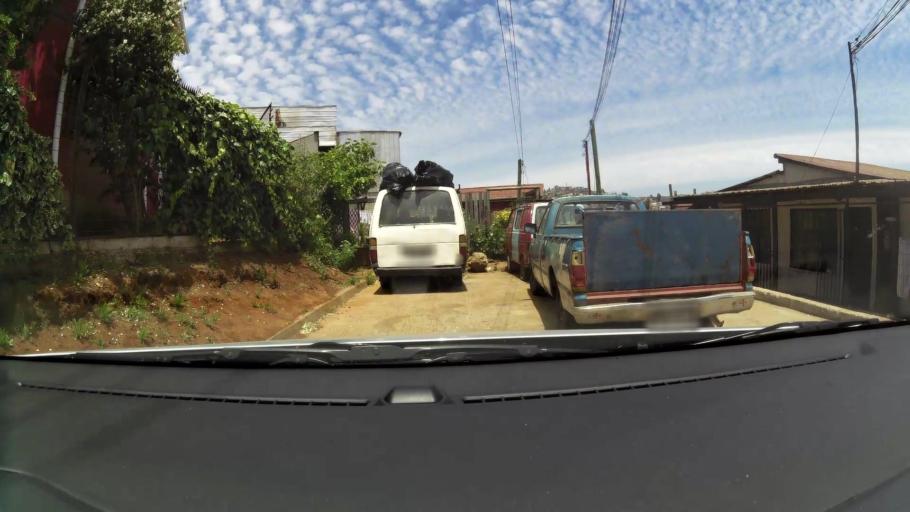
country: CL
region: Valparaiso
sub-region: Provincia de Valparaiso
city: Vina del Mar
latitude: -33.0514
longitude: -71.5747
